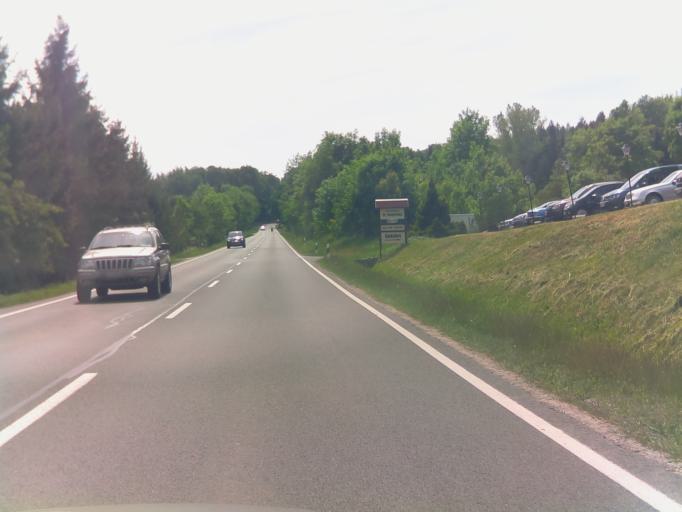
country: DE
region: Saxony-Anhalt
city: Blankenburg
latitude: 51.7603
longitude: 10.9585
